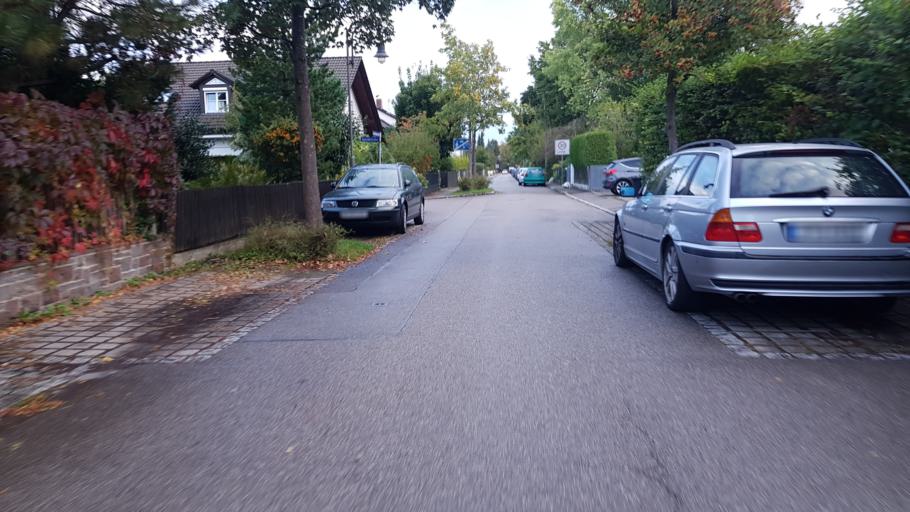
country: DE
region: Bavaria
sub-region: Upper Bavaria
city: Ottobrunn
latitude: 48.0763
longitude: 11.6739
